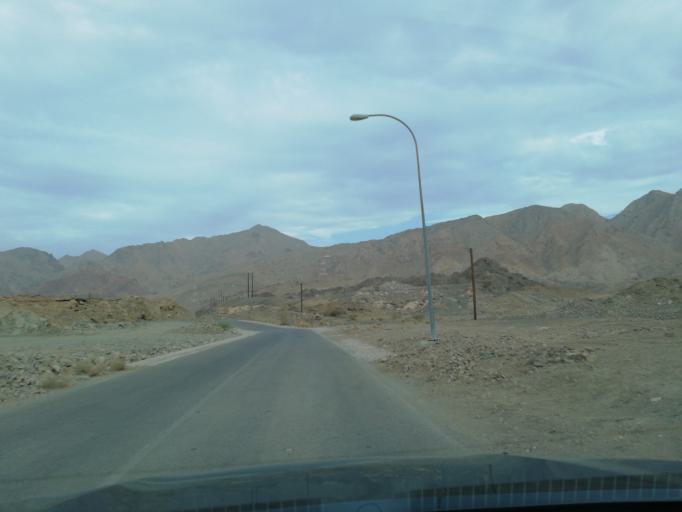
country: OM
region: Muhafazat Masqat
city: Bawshar
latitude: 23.4881
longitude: 58.3337
